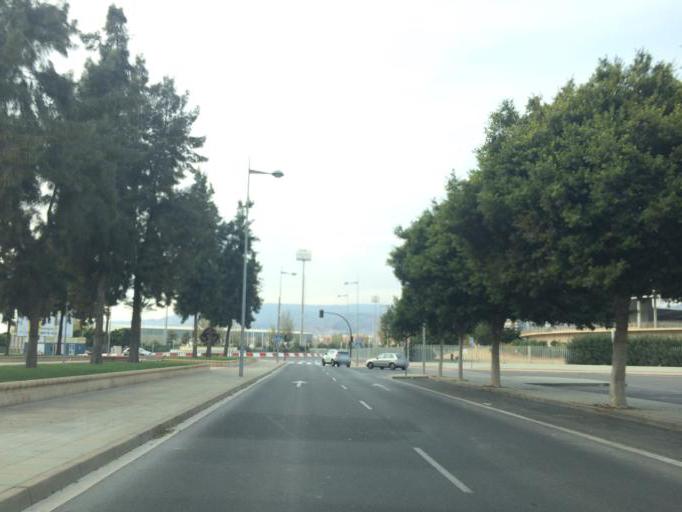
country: ES
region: Andalusia
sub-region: Provincia de Almeria
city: Almeria
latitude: 36.8382
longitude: -2.4344
